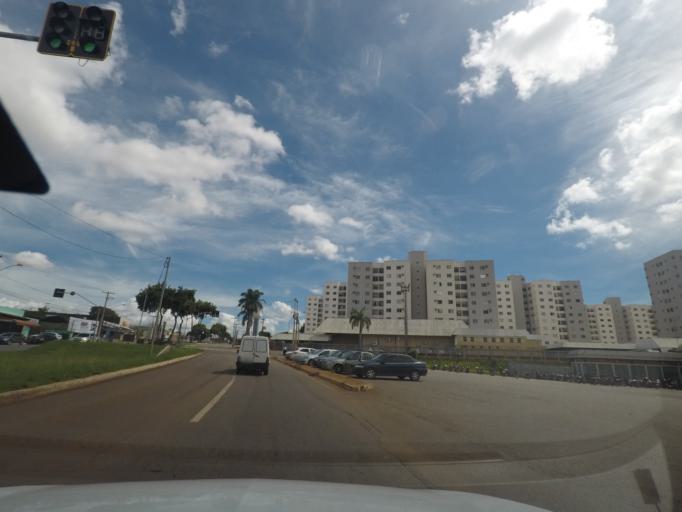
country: BR
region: Goias
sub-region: Goiania
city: Goiania
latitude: -16.7318
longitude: -49.3254
